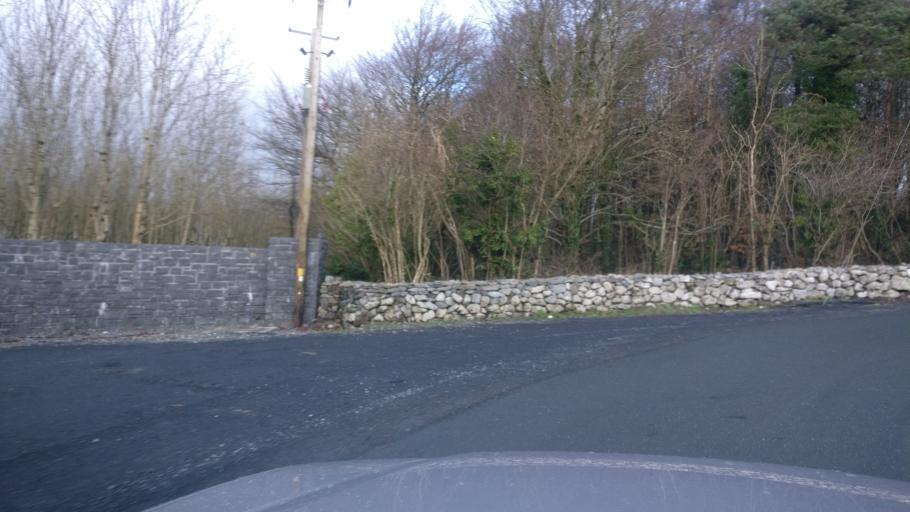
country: IE
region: Connaught
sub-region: County Galway
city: Athenry
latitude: 53.2543
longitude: -8.7240
